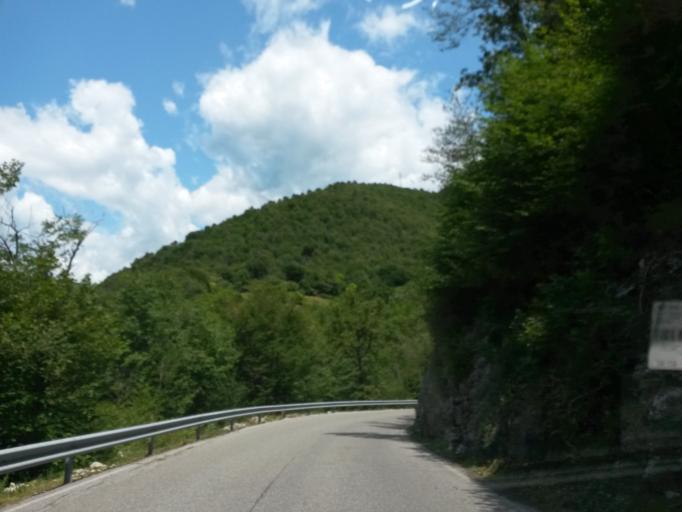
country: IT
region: Lombardy
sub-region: Provincia di Brescia
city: Gargnano
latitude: 45.6853
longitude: 10.6138
